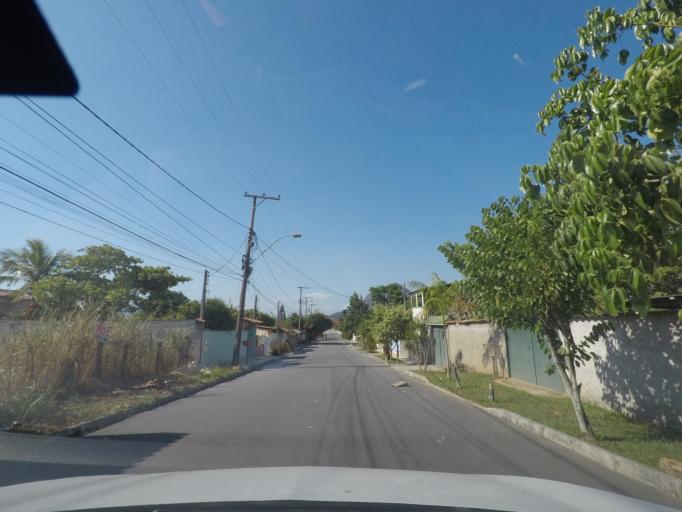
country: BR
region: Rio de Janeiro
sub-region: Marica
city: Marica
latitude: -22.9682
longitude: -42.9199
